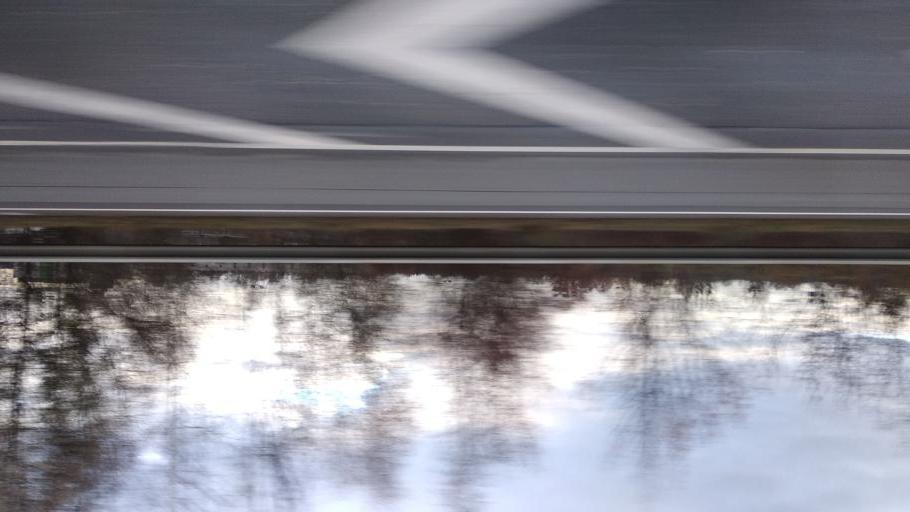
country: AT
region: Vorarlberg
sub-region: Politischer Bezirk Bregenz
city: Lauterach
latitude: 47.4607
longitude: 9.7243
